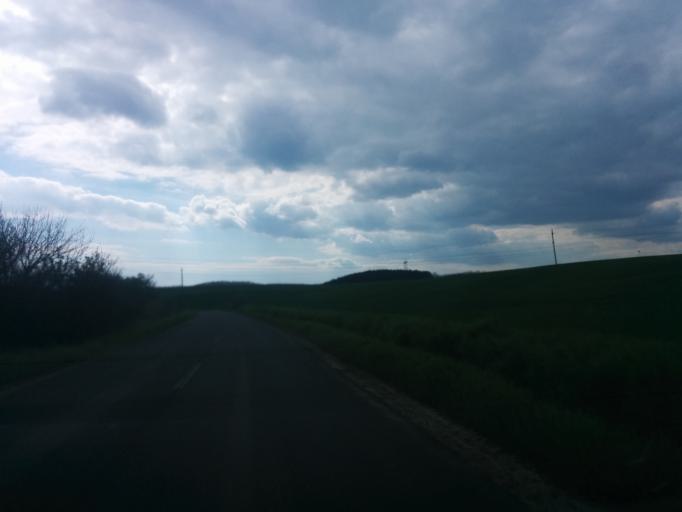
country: HU
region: Nograd
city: Retsag
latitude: 47.8859
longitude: 19.1750
